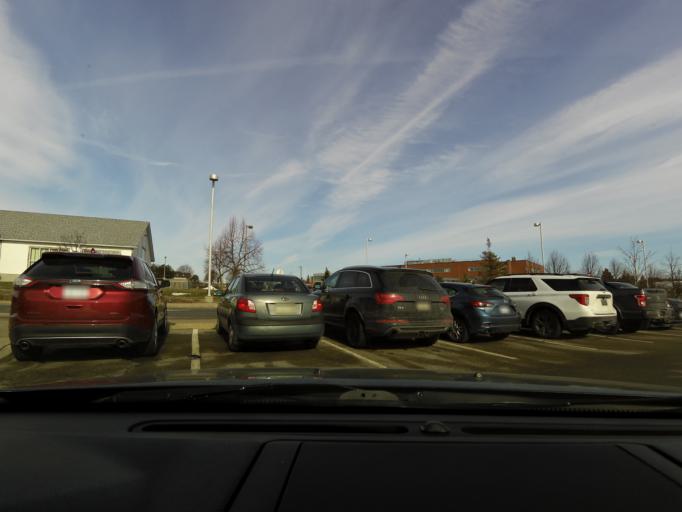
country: CA
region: Ontario
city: Brampton
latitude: 43.7491
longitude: -79.7416
